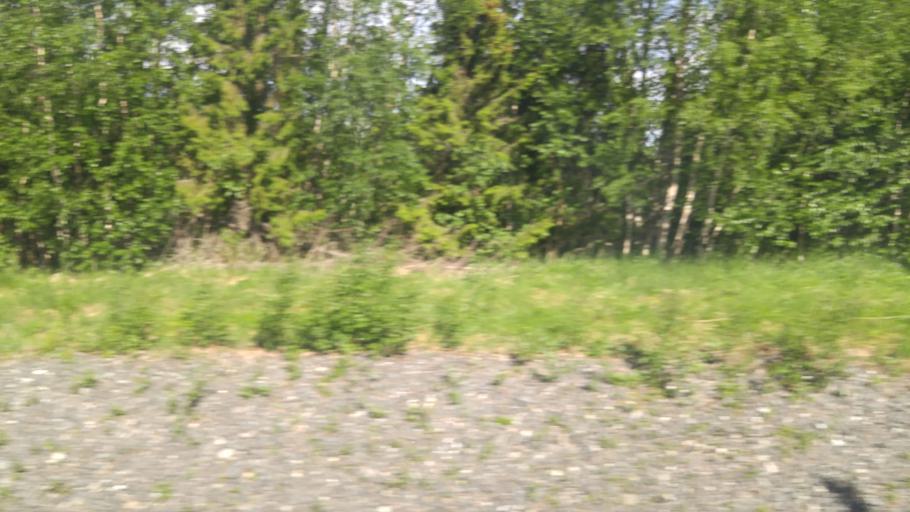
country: SE
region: Jaemtland
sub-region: Are Kommun
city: Are
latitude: 63.3677
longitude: 12.7134
